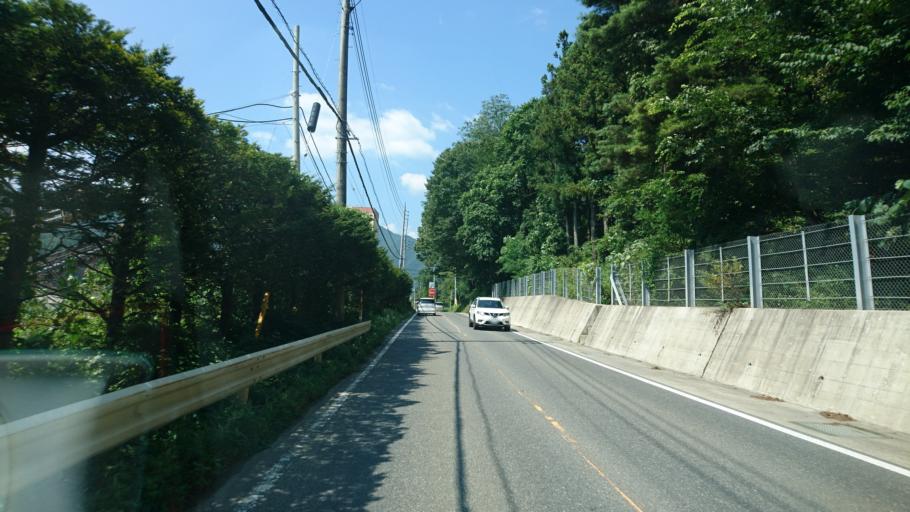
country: JP
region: Gunma
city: Numata
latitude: 36.7500
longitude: 139.2328
